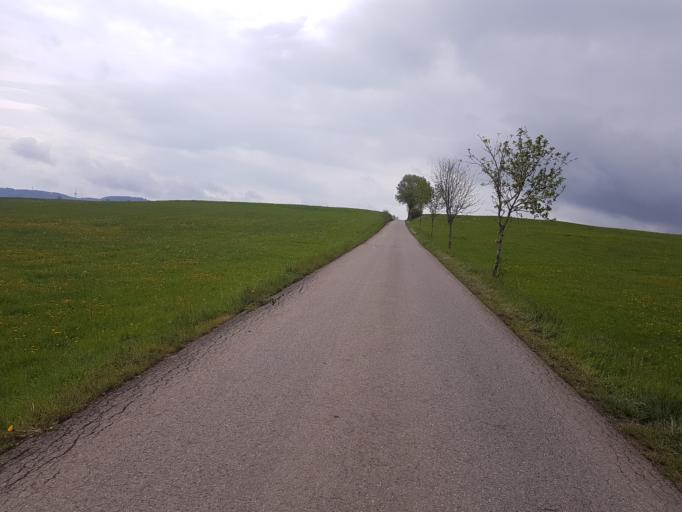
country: DE
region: Baden-Wuerttemberg
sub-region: Freiburg Region
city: Hufingen
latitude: 47.9123
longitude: 8.5185
